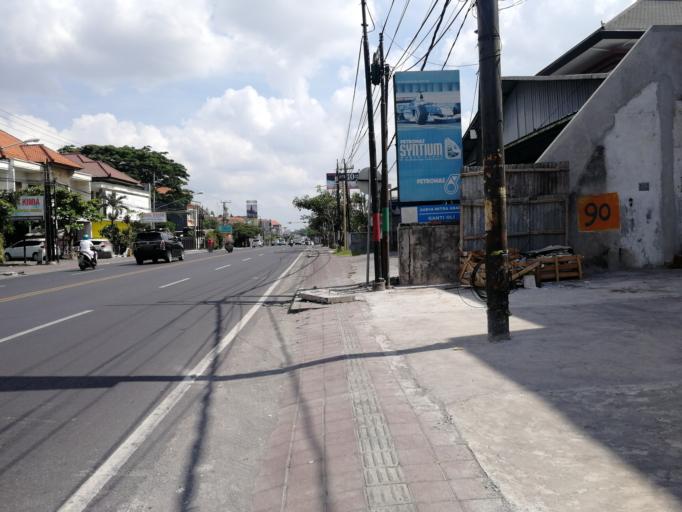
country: ID
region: Bali
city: Denpasar
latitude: -8.6427
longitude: 115.1963
